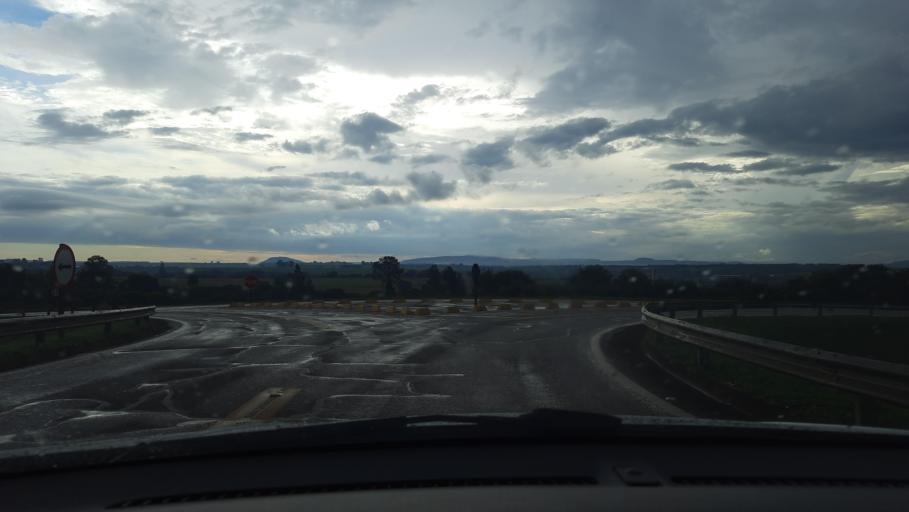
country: BR
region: Sao Paulo
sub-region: Casa Branca
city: Casa Branca
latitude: -21.7490
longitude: -47.0721
